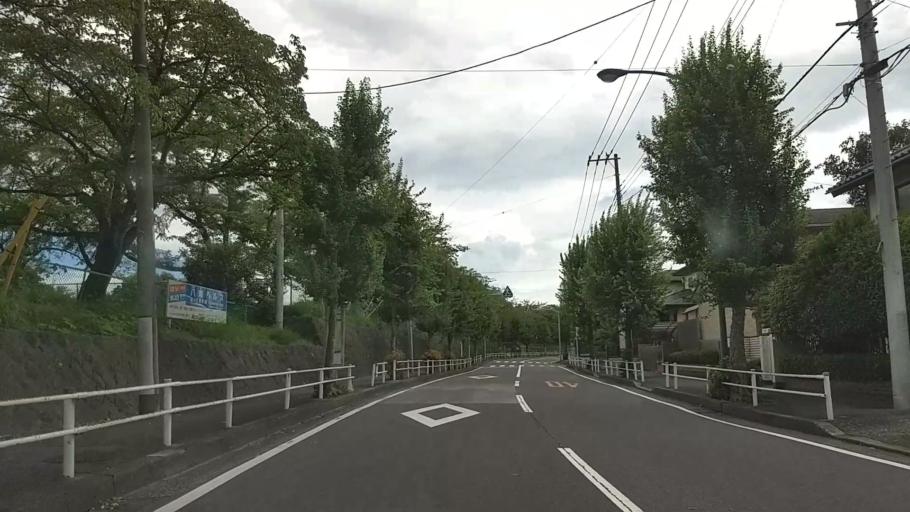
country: JP
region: Tokyo
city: Hachioji
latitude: 35.6308
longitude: 139.3580
